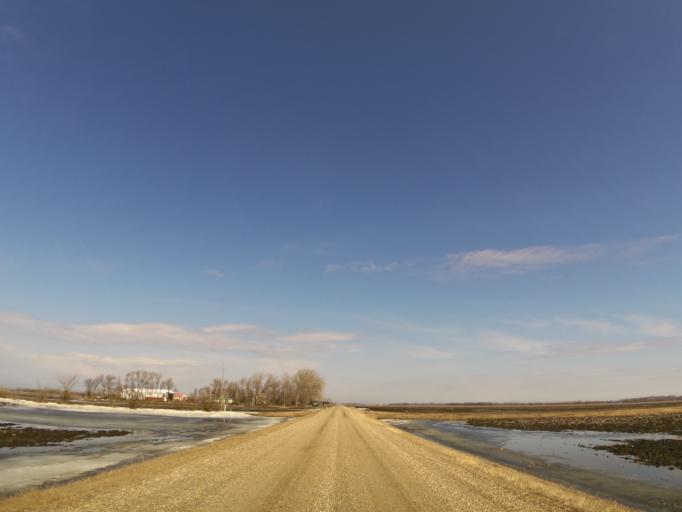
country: US
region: North Dakota
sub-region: Walsh County
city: Grafton
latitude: 48.4040
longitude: -97.1685
